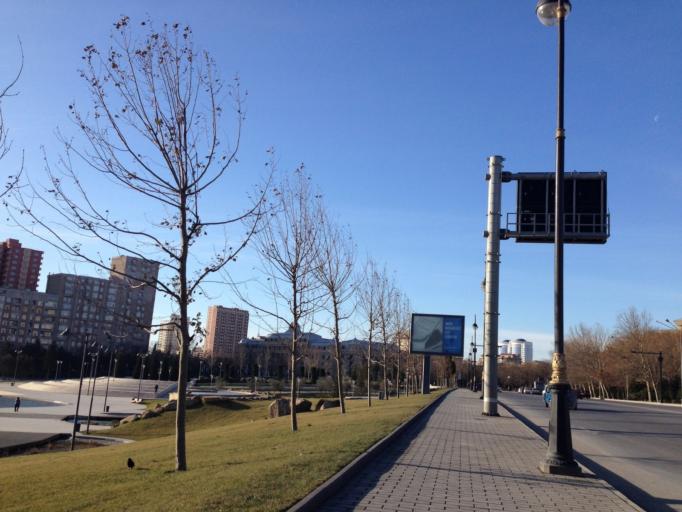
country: AZ
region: Baki
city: Baku
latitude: 40.3943
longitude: 49.8472
